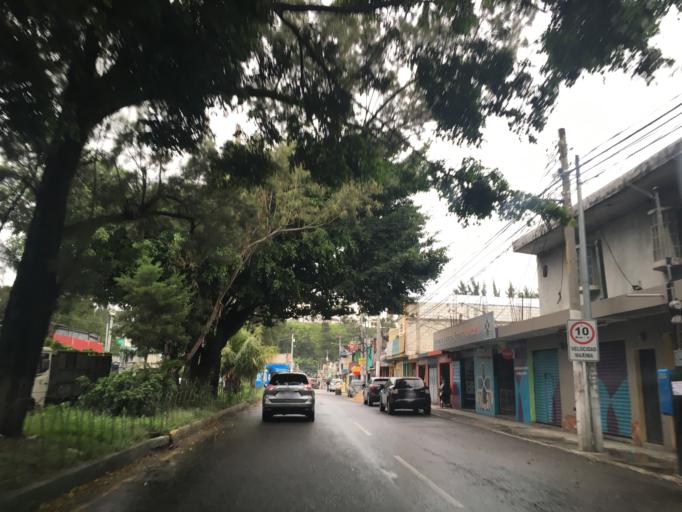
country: GT
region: Guatemala
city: Petapa
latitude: 14.5225
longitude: -90.5475
